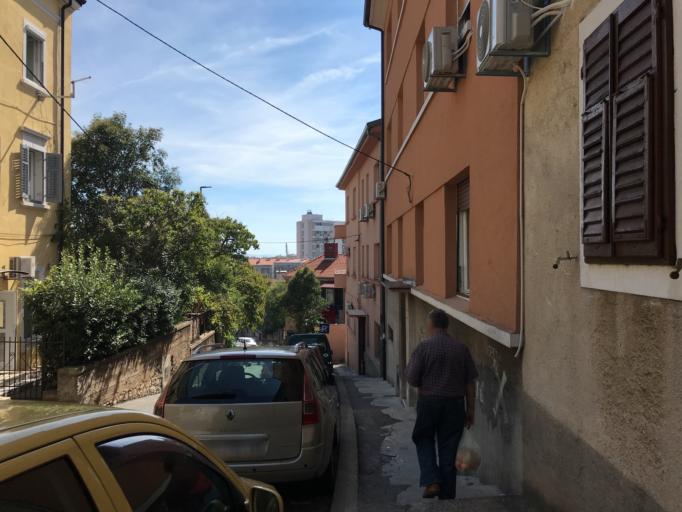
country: HR
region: Primorsko-Goranska
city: Drenova
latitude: 45.3342
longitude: 14.4294
